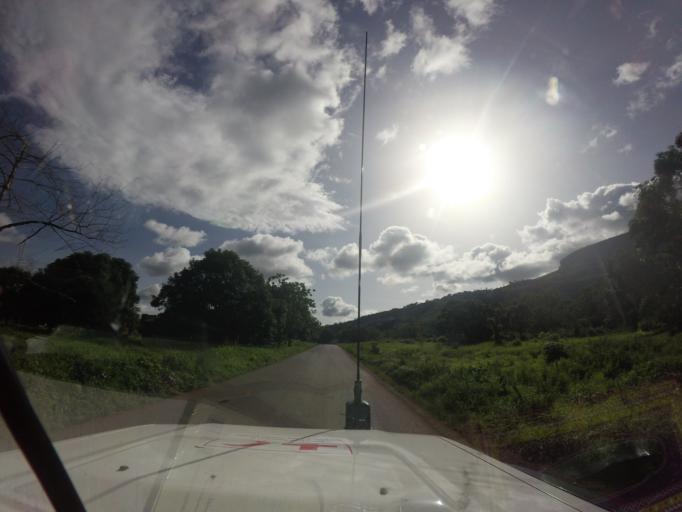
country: GN
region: Kindia
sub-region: Kindia
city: Kindia
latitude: 10.1776
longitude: -12.5043
